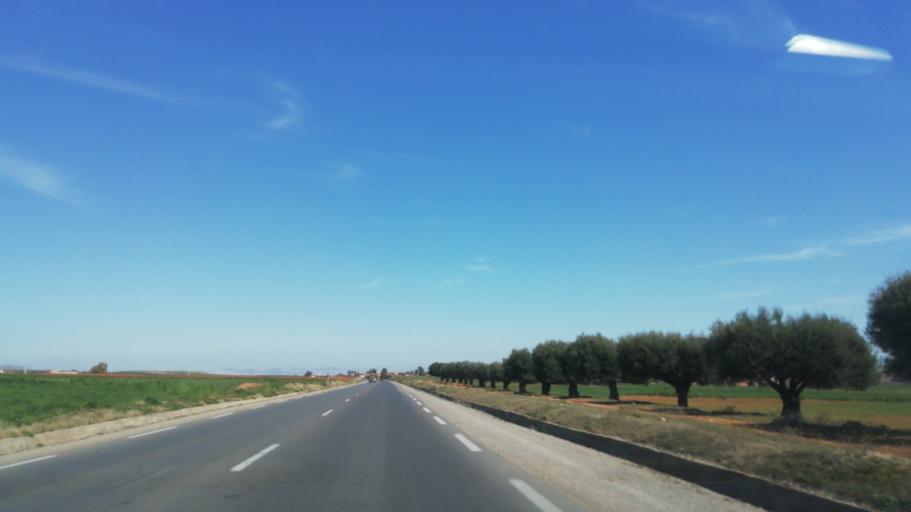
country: DZ
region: Mascara
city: Oued el Abtal
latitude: 35.4214
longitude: 0.4393
